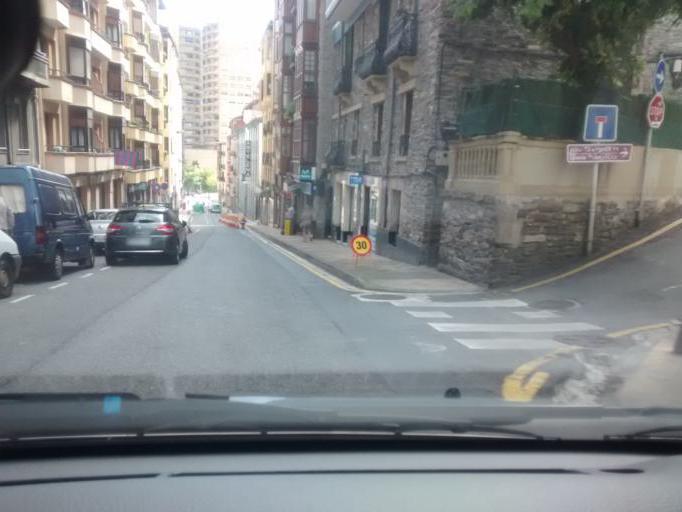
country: ES
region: Basque Country
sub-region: Provincia de Guipuzcoa
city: Eibar
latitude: 43.1837
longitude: -2.4757
